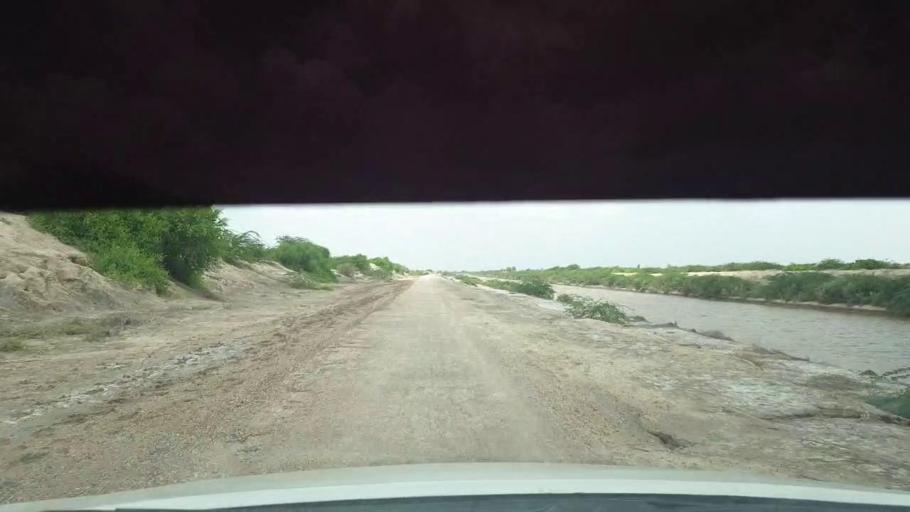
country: PK
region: Sindh
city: Kadhan
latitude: 24.5100
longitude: 69.1190
